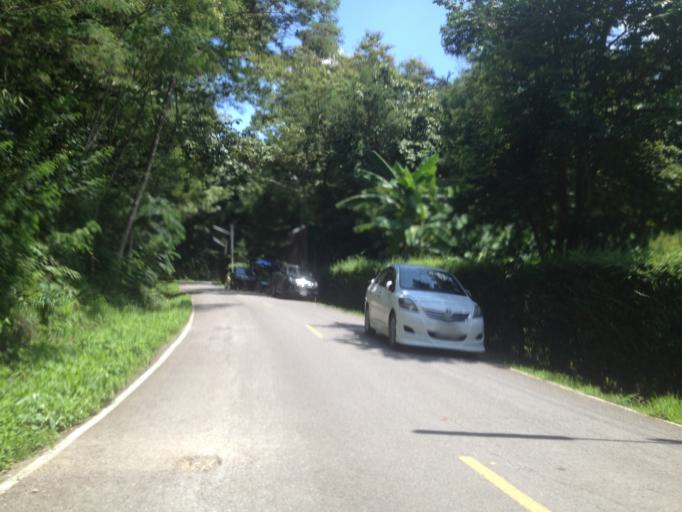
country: TH
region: Chiang Mai
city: Chiang Mai
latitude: 18.7606
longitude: 98.9227
